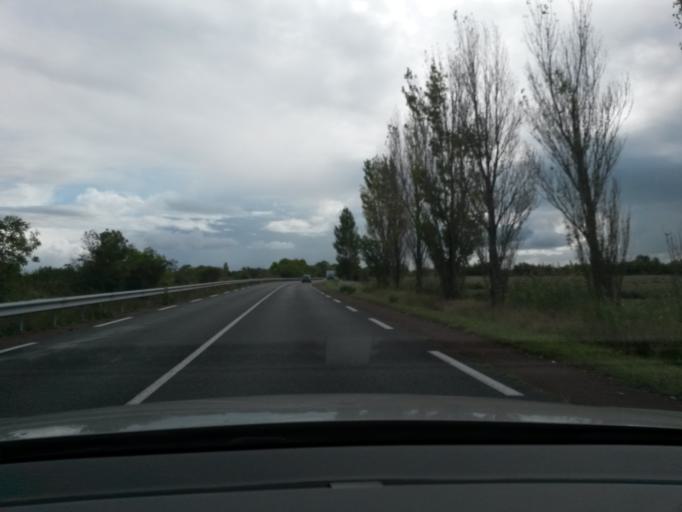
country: FR
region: Poitou-Charentes
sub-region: Departement de la Charente-Maritime
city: Saint-Just-Luzac
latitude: 45.8243
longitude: -1.0507
